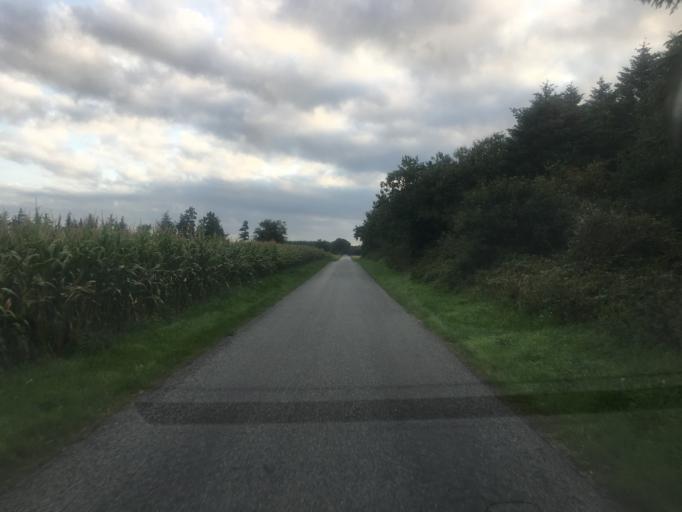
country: DK
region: South Denmark
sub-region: Tonder Kommune
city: Logumkloster
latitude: 55.0348
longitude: 8.9235
